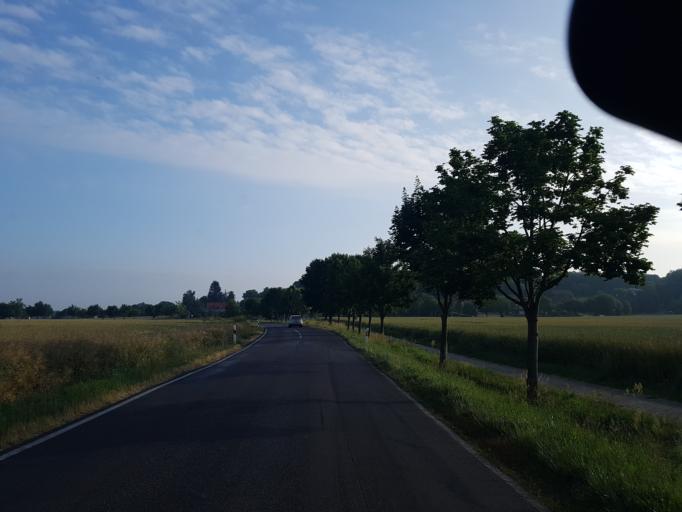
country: DE
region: Brandenburg
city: Schlieben
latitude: 51.7158
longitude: 13.3844
